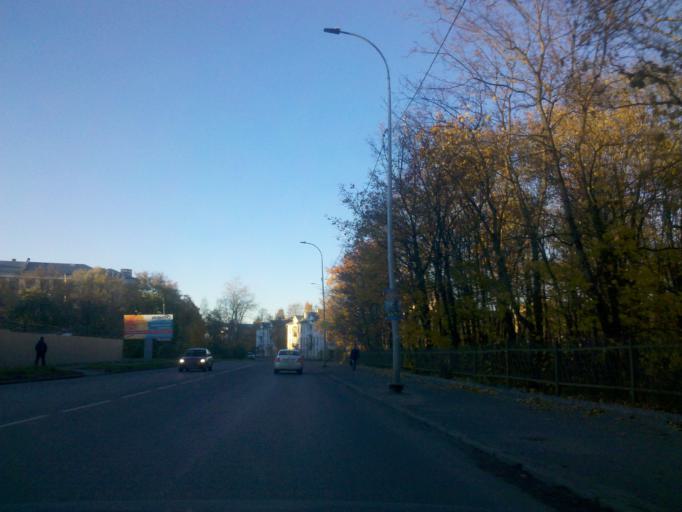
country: RU
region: Republic of Karelia
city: Petrozavodsk
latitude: 61.7794
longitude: 34.3891
